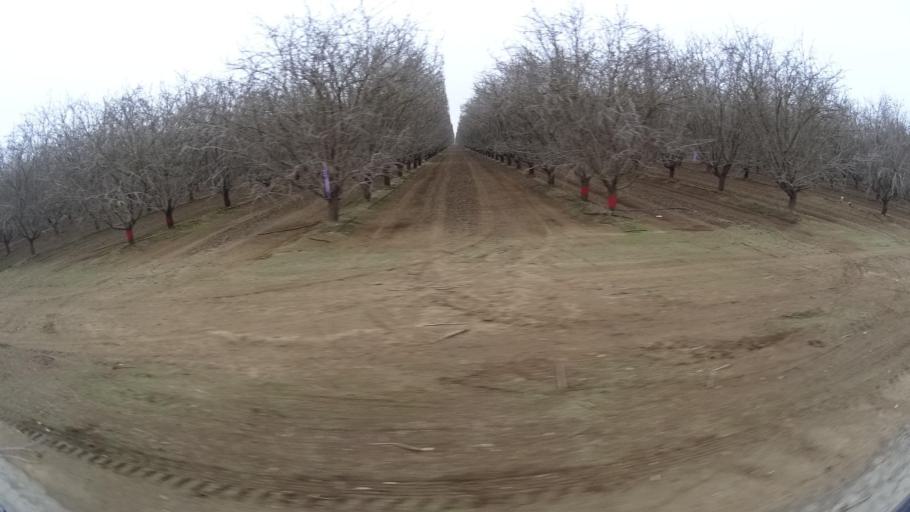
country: US
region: California
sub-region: Kern County
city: Wasco
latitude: 35.5721
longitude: -119.4885
